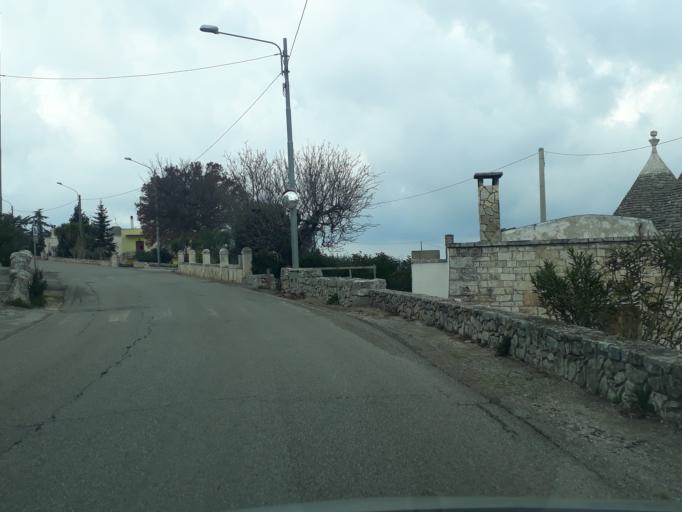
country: IT
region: Apulia
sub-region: Provincia di Brindisi
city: Lamie di Olimpie-Selva
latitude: 40.7900
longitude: 17.3225
